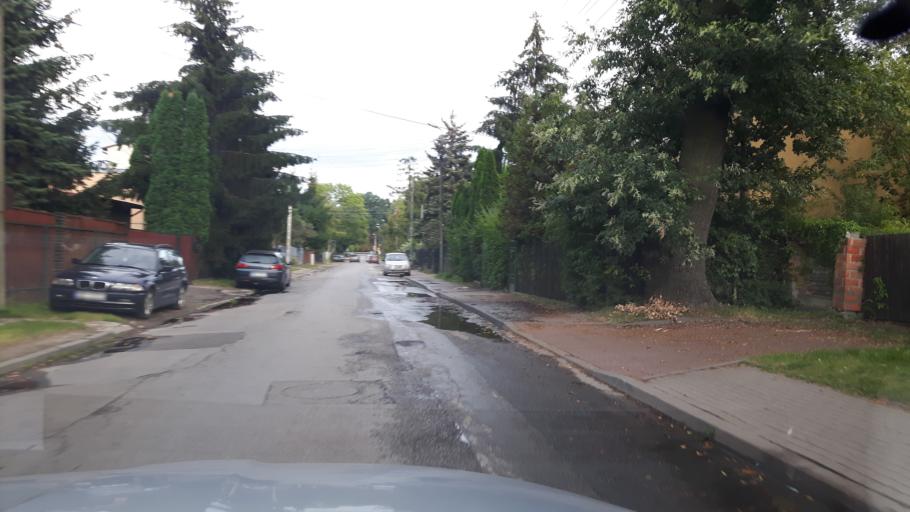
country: PL
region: Masovian Voivodeship
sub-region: Powiat wolominski
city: Marki
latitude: 52.3243
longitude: 21.1006
